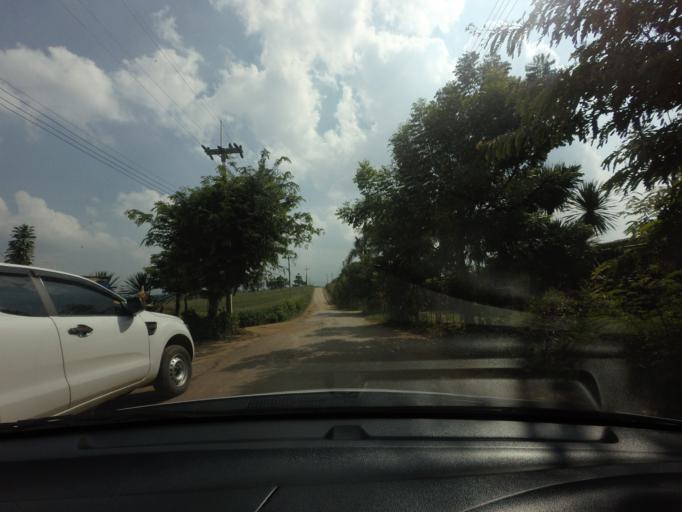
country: TH
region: Nakhon Ratchasima
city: Pak Chong
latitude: 14.5261
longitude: 101.5745
